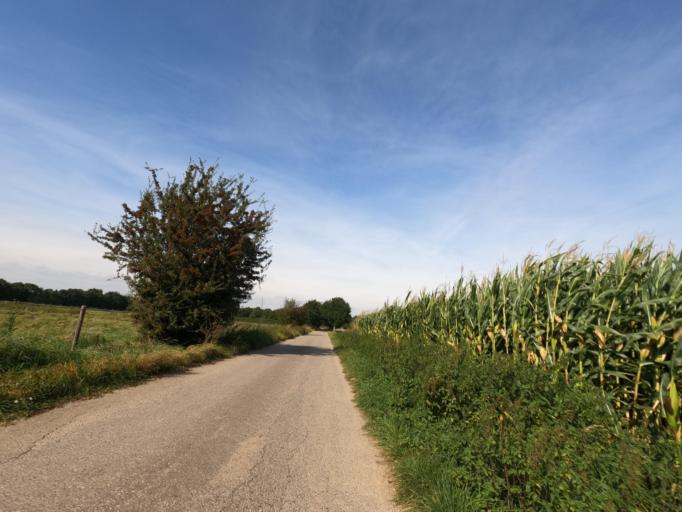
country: DE
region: North Rhine-Westphalia
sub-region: Regierungsbezirk Koln
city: Linnich
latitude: 50.9736
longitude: 6.2914
